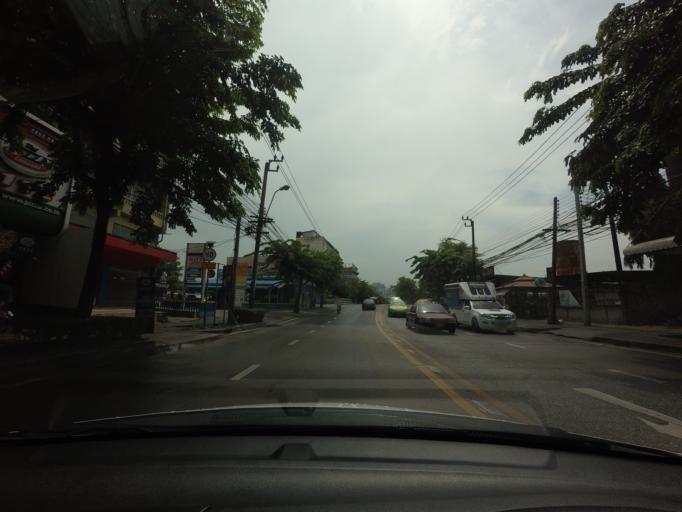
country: TH
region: Bangkok
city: Phra Khanong
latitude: 13.7089
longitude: 100.6169
